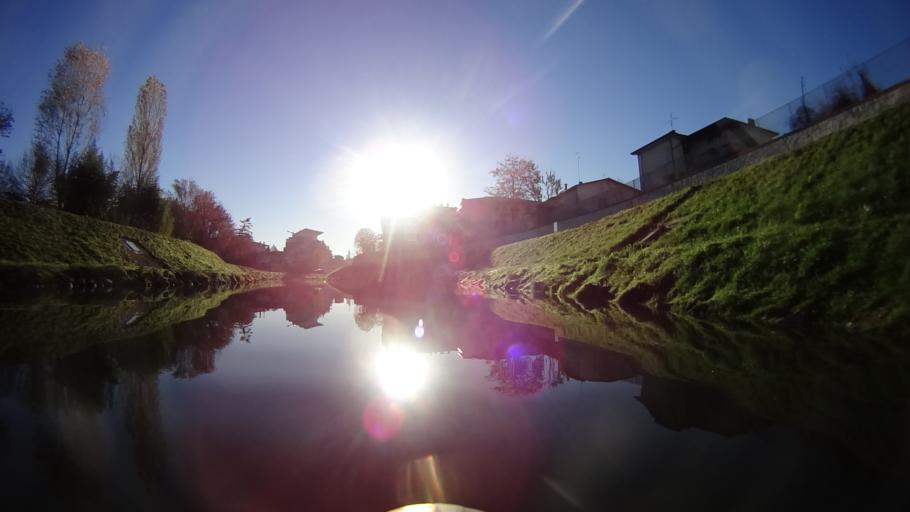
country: IT
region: Veneto
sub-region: Provincia di Vicenza
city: Vicenza
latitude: 45.5573
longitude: 11.5312
